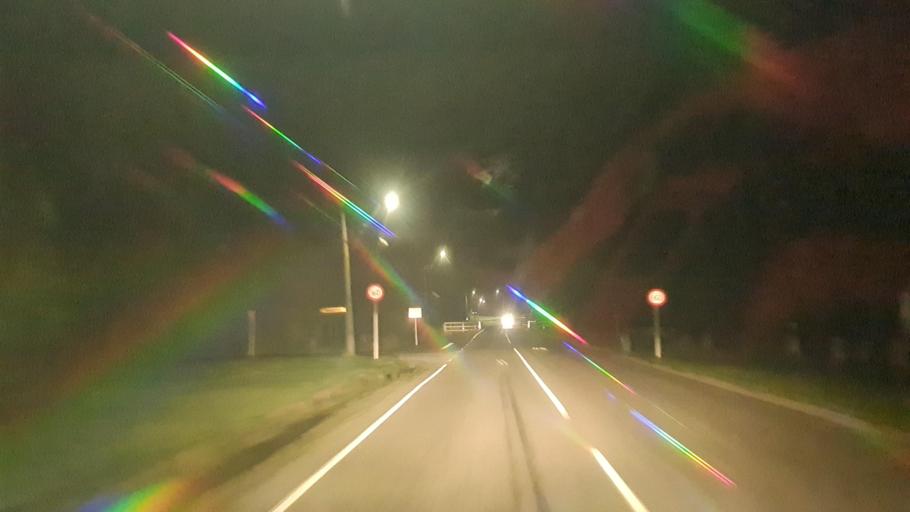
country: NZ
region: Otago
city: Oamaru
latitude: -45.0987
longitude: 170.9394
